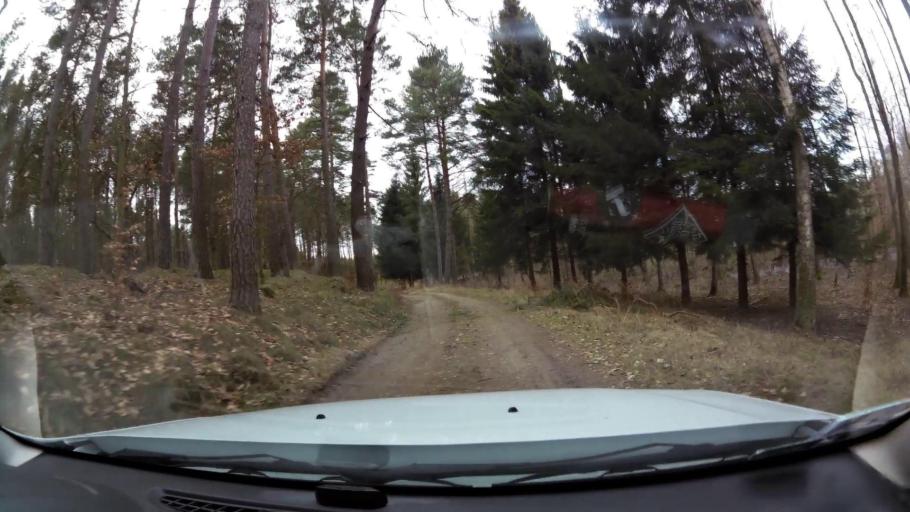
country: PL
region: West Pomeranian Voivodeship
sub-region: Powiat drawski
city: Drawsko Pomorskie
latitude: 53.5330
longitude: 15.6993
